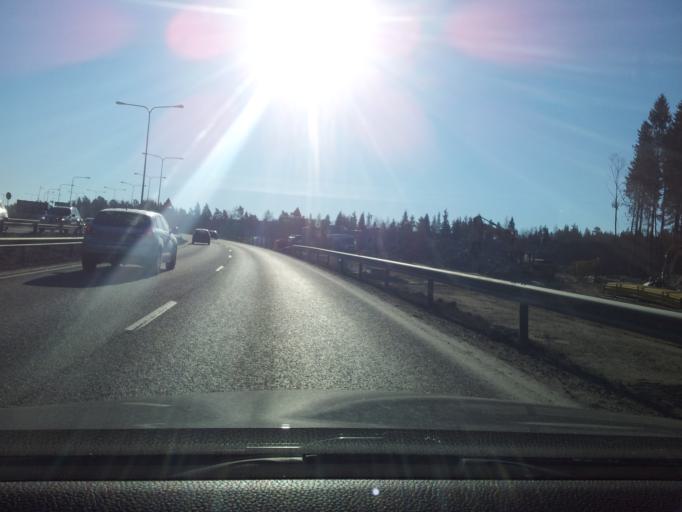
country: FI
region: Uusimaa
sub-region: Helsinki
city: Vantaa
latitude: 60.2315
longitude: 25.0508
